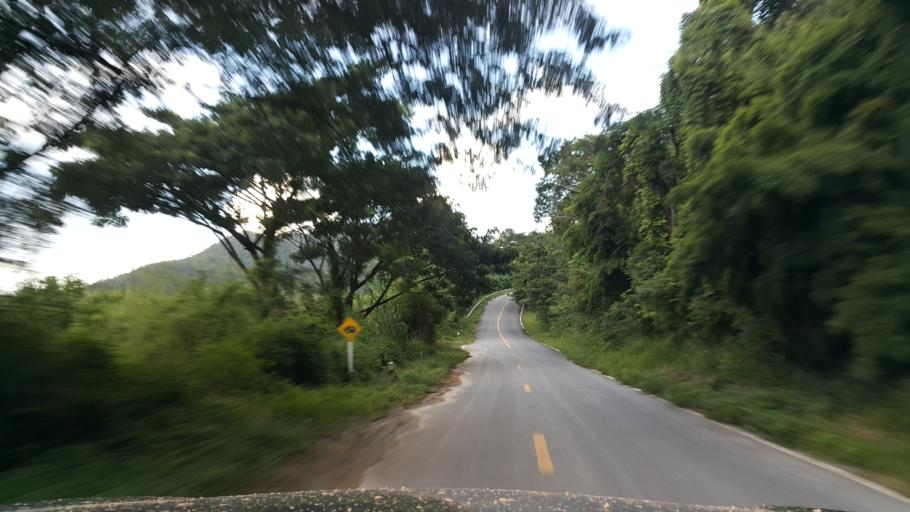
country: TH
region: Mae Hong Son
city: Mae Hi
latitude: 19.2439
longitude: 98.4530
